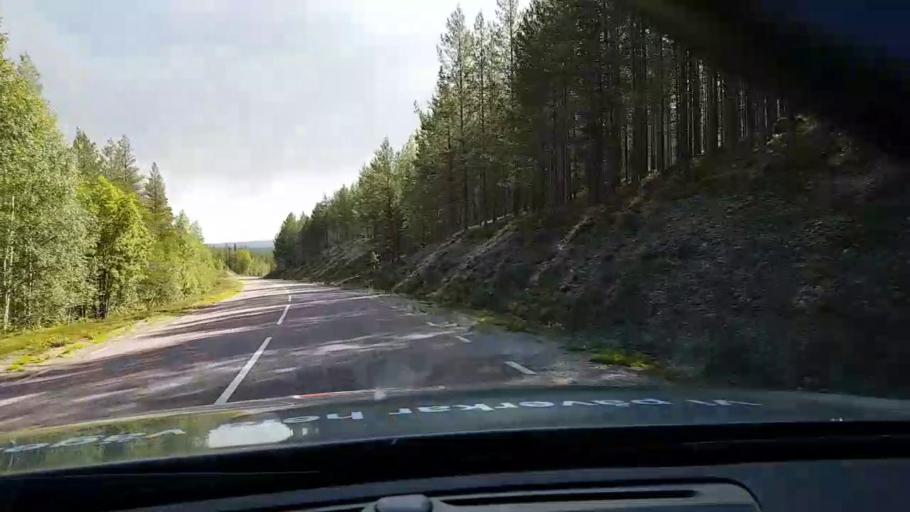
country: SE
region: Vaesterbotten
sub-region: Asele Kommun
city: Asele
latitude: 63.8806
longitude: 17.3546
